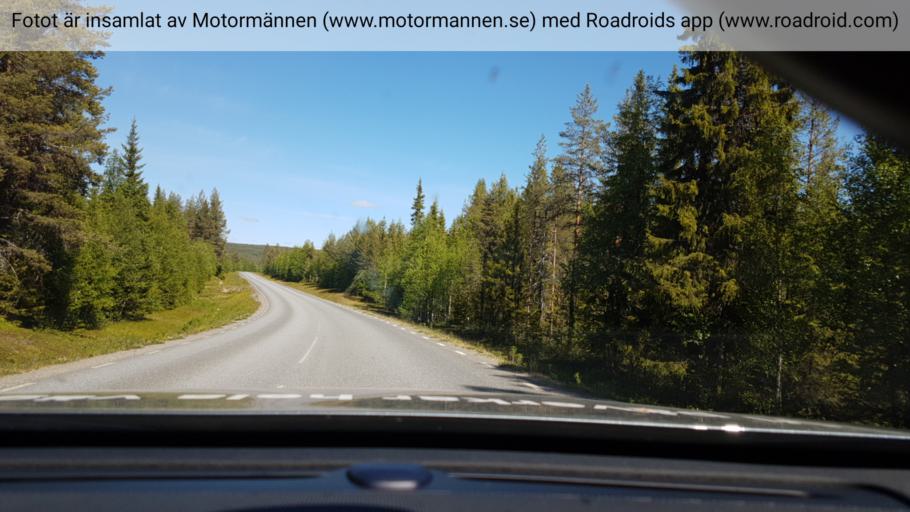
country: SE
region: Vaesterbotten
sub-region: Vilhelmina Kommun
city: Vilhelmina
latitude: 64.6458
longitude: 16.9721
